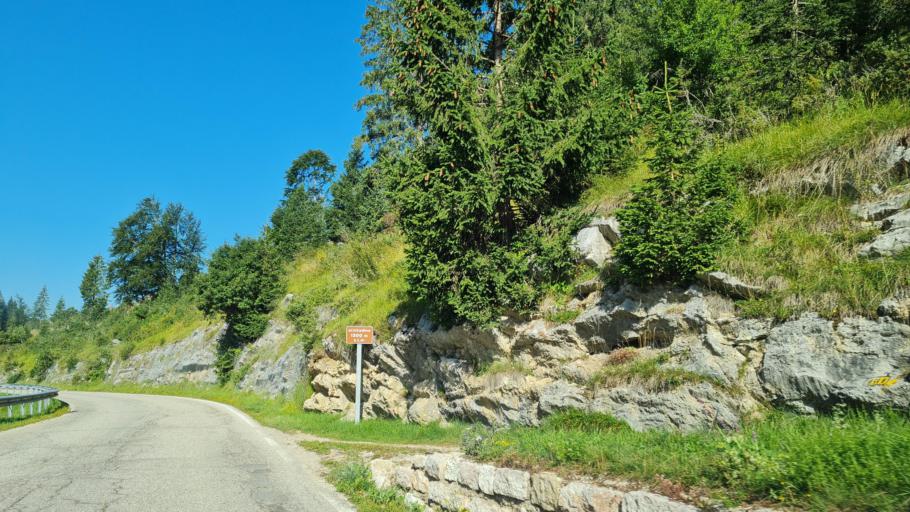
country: IT
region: Veneto
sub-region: Provincia di Vicenza
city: San Pietro Valdastico
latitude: 45.9518
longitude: 11.3869
